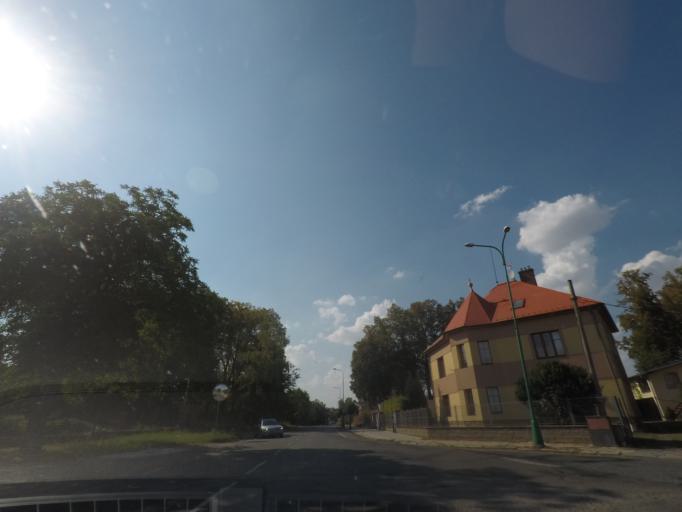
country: CZ
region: Kralovehradecky
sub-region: Okres Nachod
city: Jaromer
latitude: 50.3352
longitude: 15.9356
